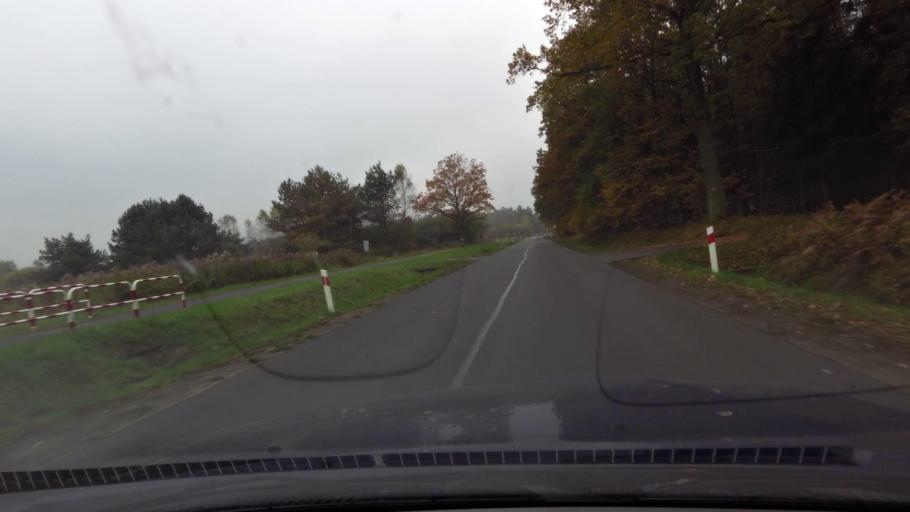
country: PL
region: West Pomeranian Voivodeship
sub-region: Powiat goleniowski
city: Goleniow
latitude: 53.5770
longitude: 14.8004
